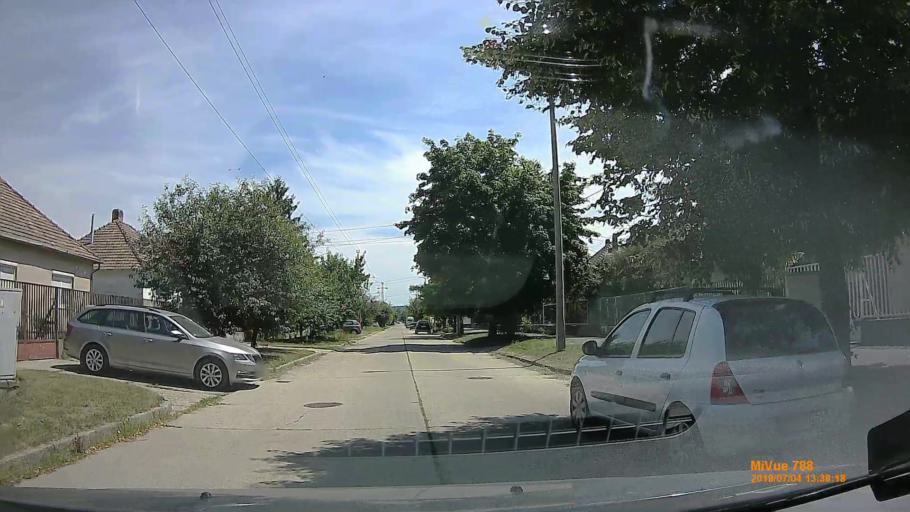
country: HU
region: Komarom-Esztergom
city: Tatabanya
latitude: 47.5716
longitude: 18.3839
